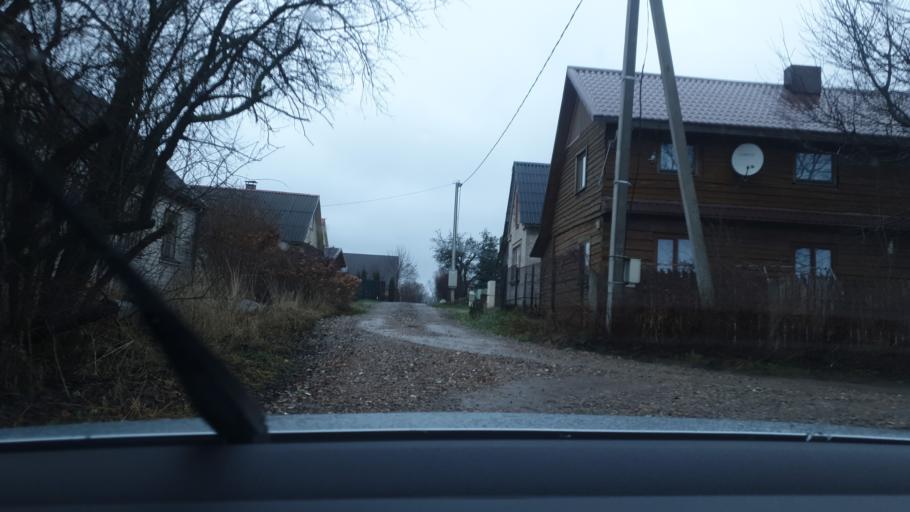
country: LT
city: Skaidiskes
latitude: 54.7055
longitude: 25.4032
